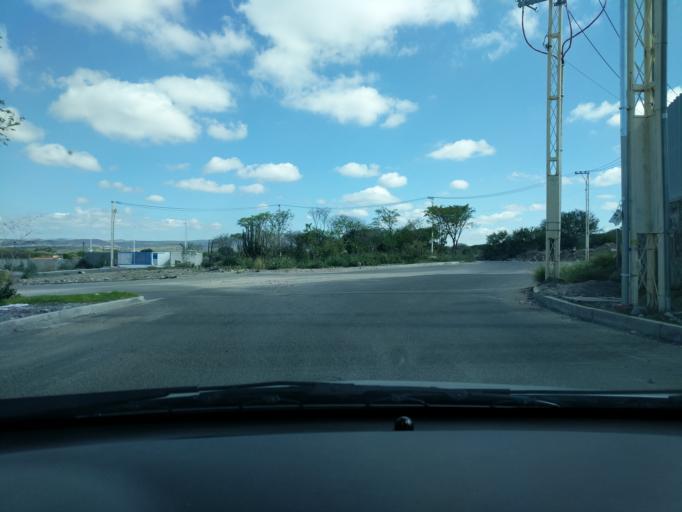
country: MX
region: Queretaro
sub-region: Queretaro
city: Patria Nueva
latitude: 20.6479
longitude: -100.4838
